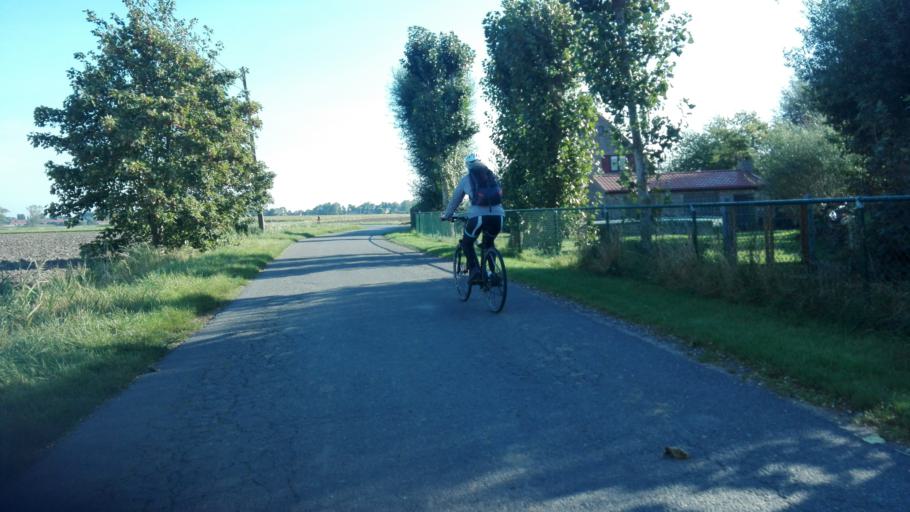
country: BE
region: Flanders
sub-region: Provincie West-Vlaanderen
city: Veurne
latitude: 51.0689
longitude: 2.6426
